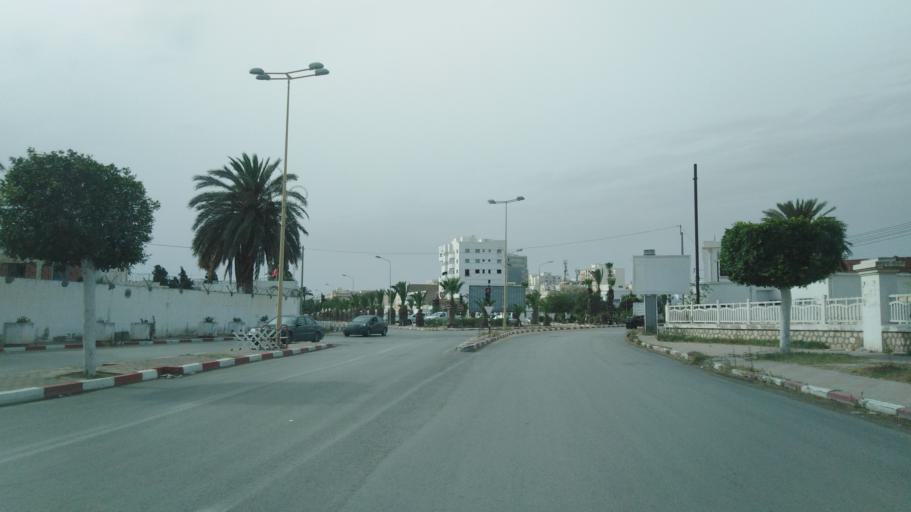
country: TN
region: Safaqis
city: Sfax
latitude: 34.7393
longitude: 10.7637
